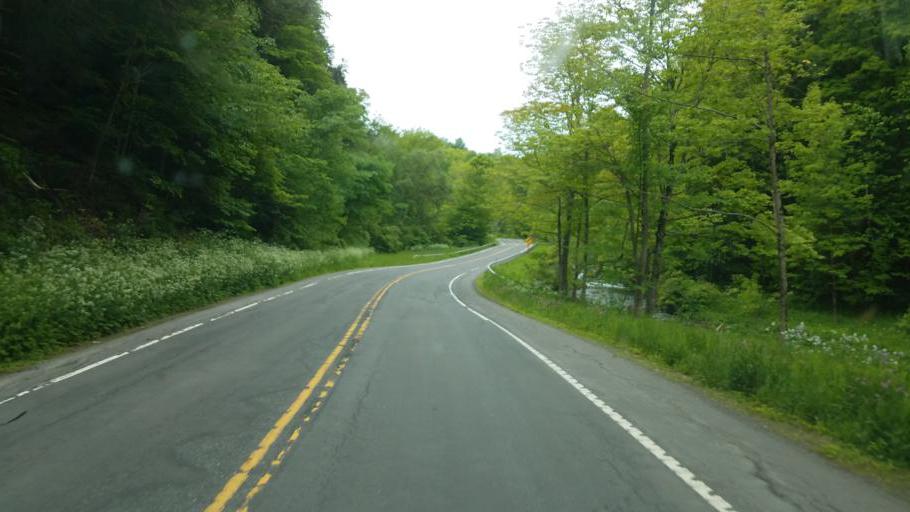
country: US
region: New York
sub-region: Herkimer County
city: Frankfort
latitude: 42.9636
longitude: -75.1023
